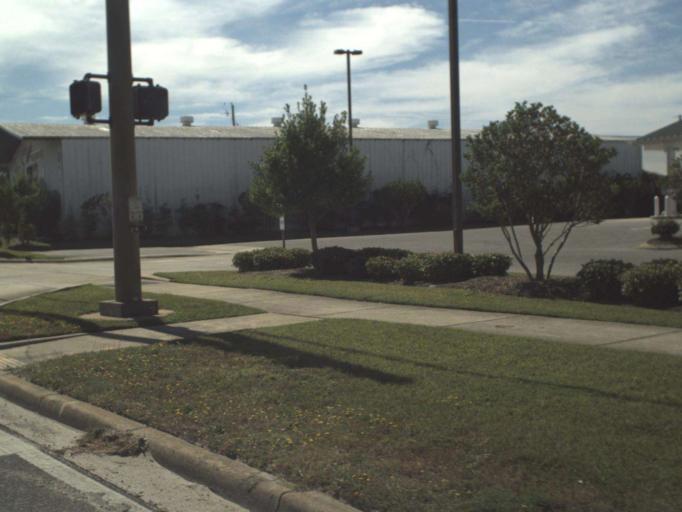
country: US
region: Florida
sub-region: Okaloosa County
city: Fort Walton Beach
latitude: 30.4156
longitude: -86.6137
